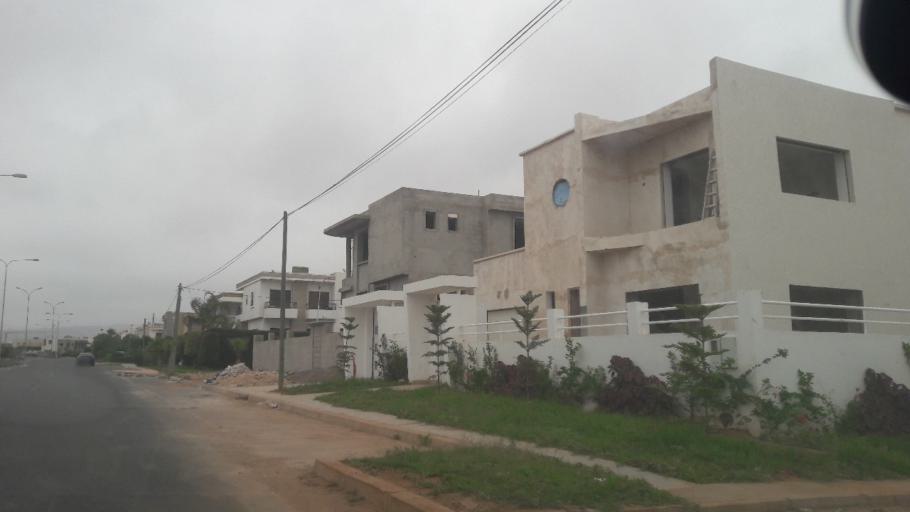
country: MA
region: Souss-Massa-Draa
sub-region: Agadir-Ida-ou-Tnan
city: Agadir
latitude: 30.3901
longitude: -9.5879
